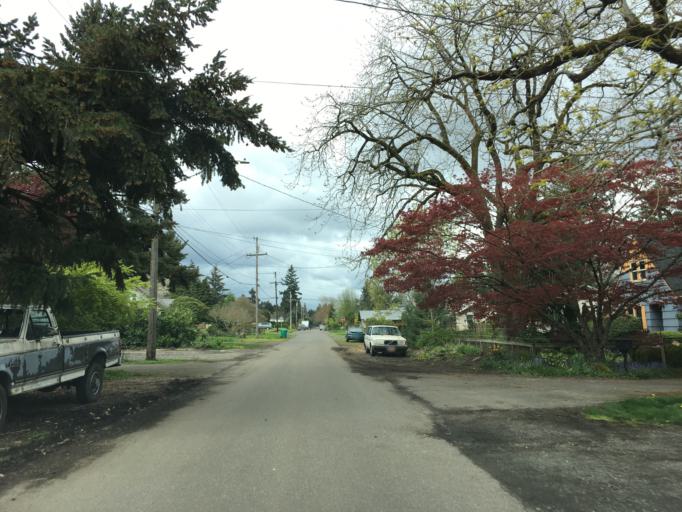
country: US
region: Oregon
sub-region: Multnomah County
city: Portland
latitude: 45.5579
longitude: -122.6031
